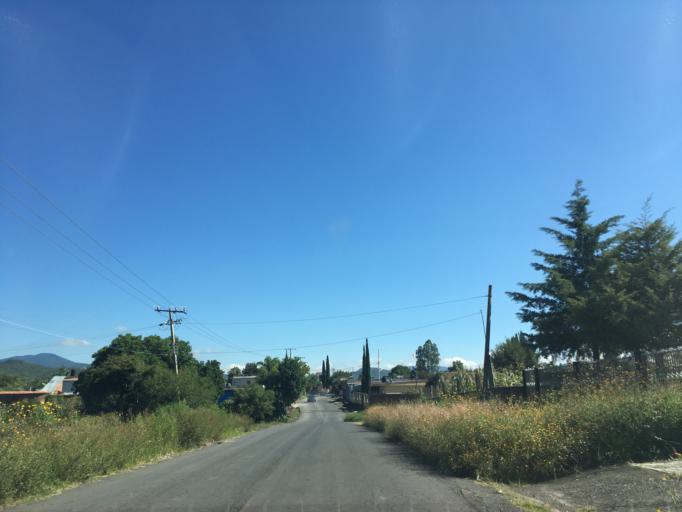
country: MX
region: Mexico
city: Tlazazalca
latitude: 19.9668
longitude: -102.1208
